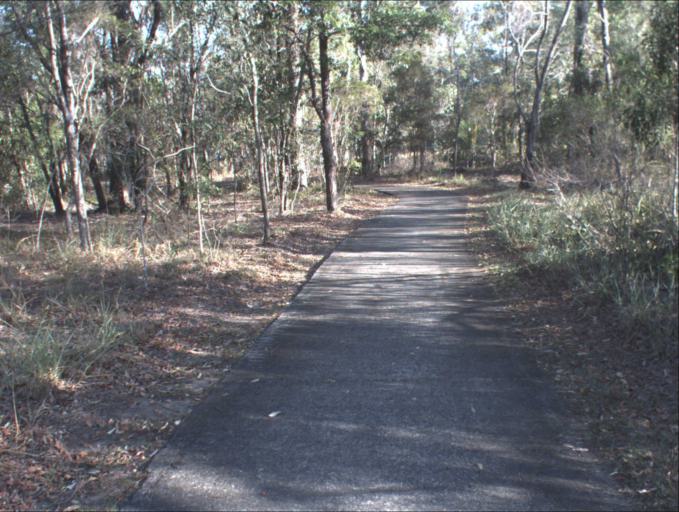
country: AU
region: Queensland
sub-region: Logan
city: Beenleigh
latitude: -27.6707
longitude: 153.2026
